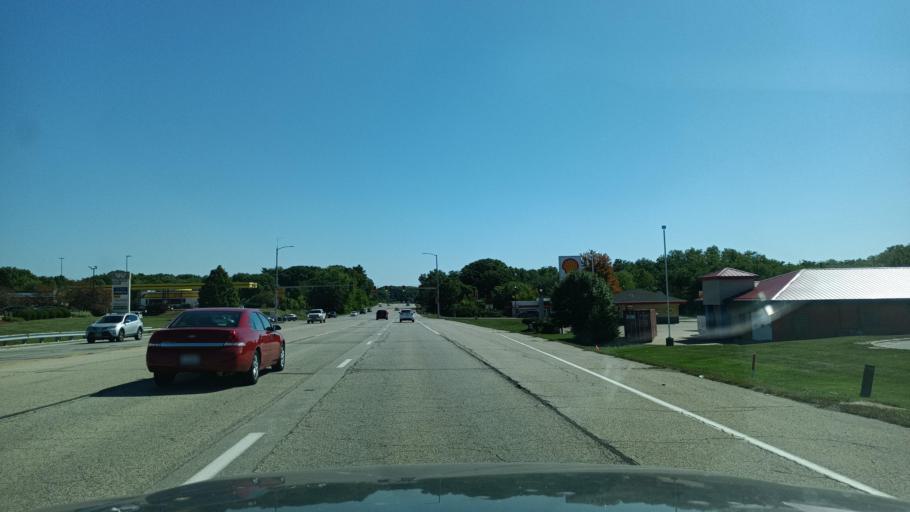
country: US
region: Illinois
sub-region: Peoria County
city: West Peoria
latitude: 40.7707
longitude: -89.6551
